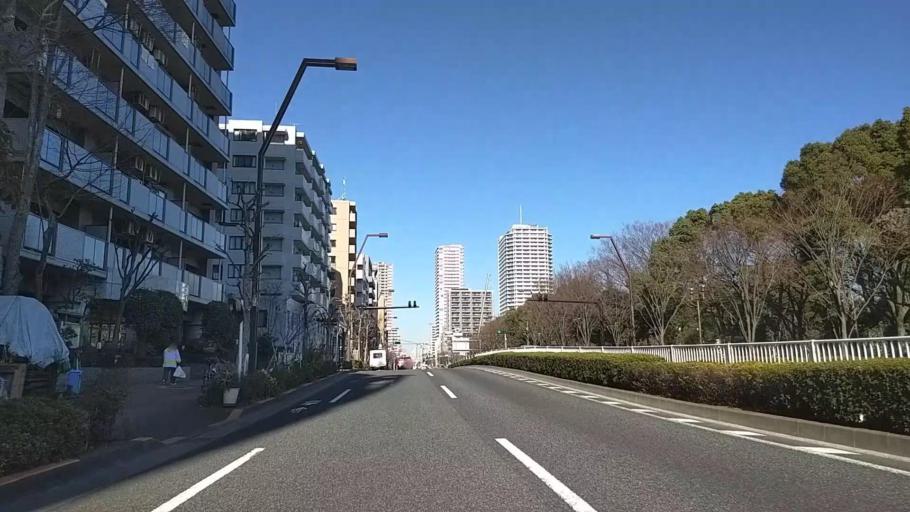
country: JP
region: Tokyo
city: Urayasu
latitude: 35.6769
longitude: 139.8070
